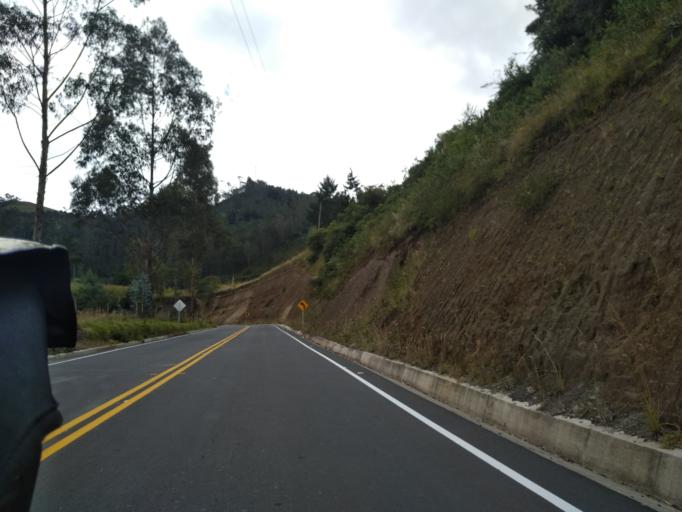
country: EC
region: Cotopaxi
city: Saquisili
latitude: -0.7255
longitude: -78.8935
